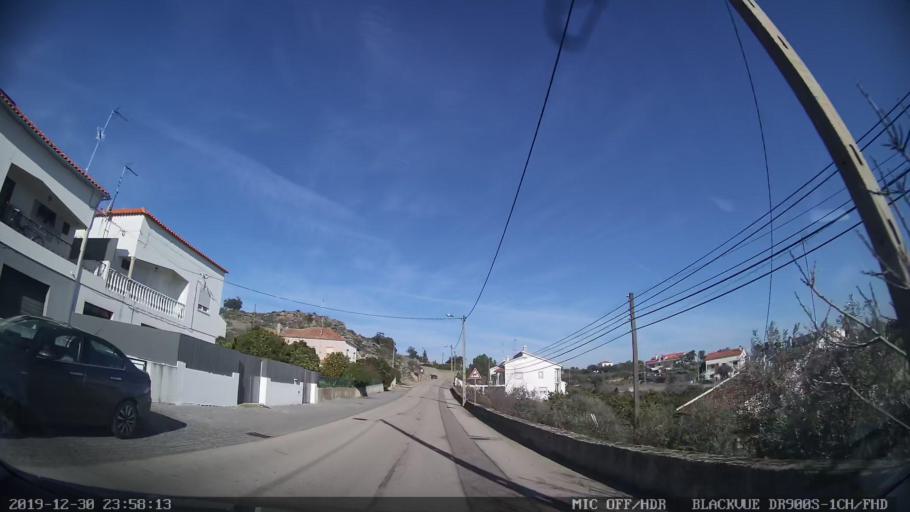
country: PT
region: Castelo Branco
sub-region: Idanha-A-Nova
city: Idanha-a-Nova
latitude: 39.9282
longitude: -7.2369
